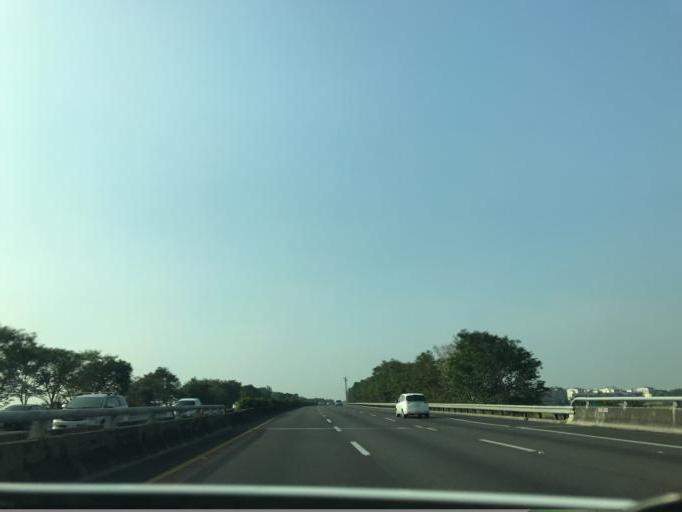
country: TW
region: Taiwan
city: Xinying
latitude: 23.3737
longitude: 120.3510
